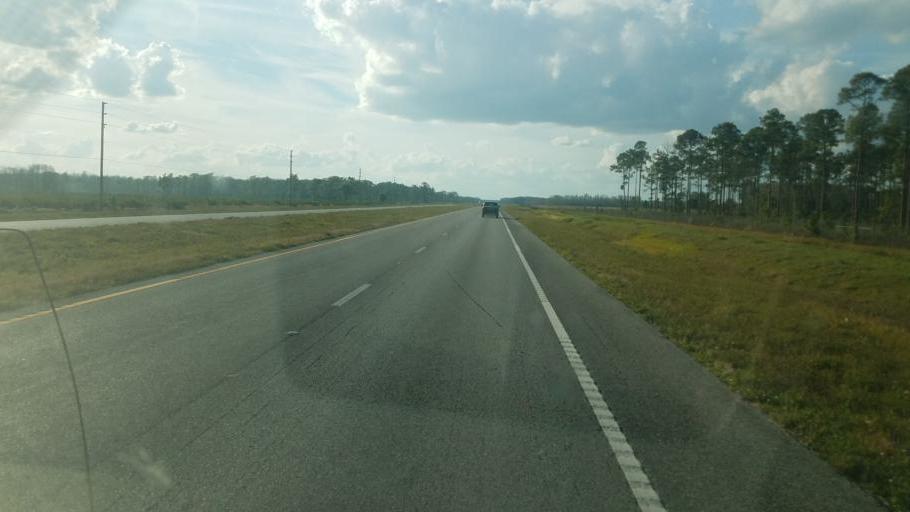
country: US
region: Florida
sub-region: Osceola County
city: Saint Cloud
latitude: 28.1380
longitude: -81.0389
